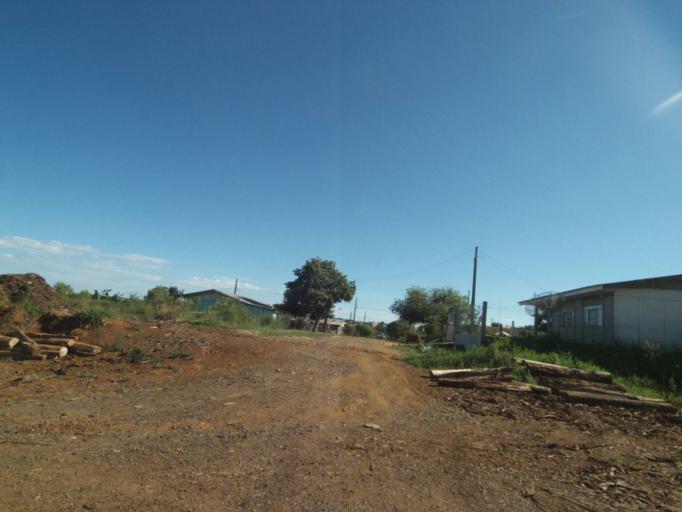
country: BR
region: Parana
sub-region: Pinhao
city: Pinhao
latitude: -25.8427
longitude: -52.0327
